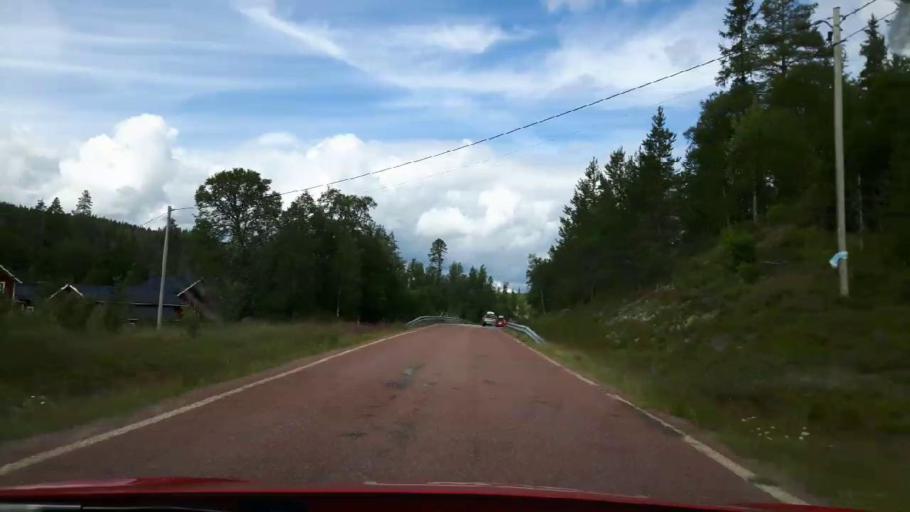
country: NO
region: Hedmark
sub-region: Trysil
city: Innbygda
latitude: 62.0002
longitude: 12.9787
